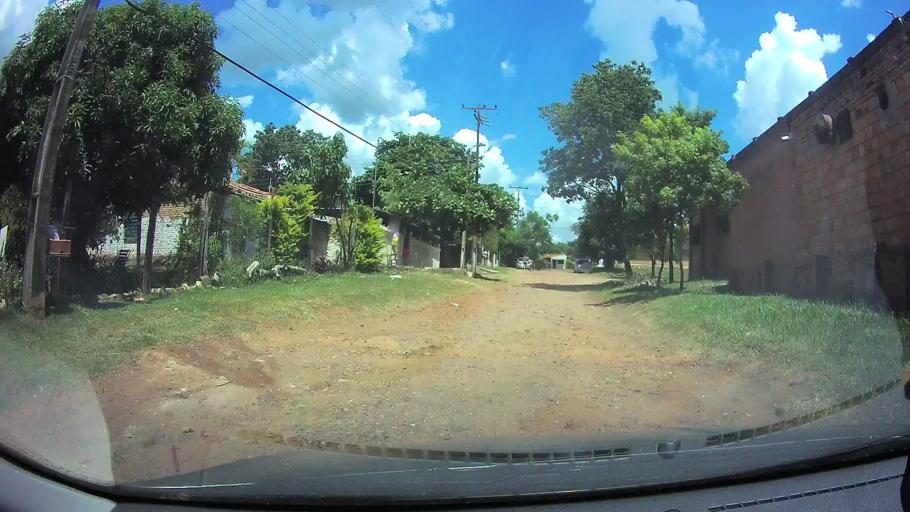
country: PY
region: Central
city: Limpio
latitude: -25.1518
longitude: -57.4475
